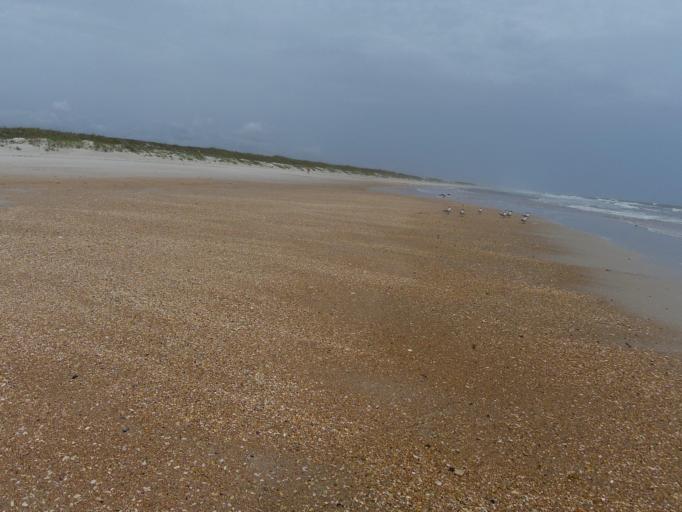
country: US
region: Florida
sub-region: Saint Johns County
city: Saint Augustine Beach
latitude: 29.8801
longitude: -81.2712
